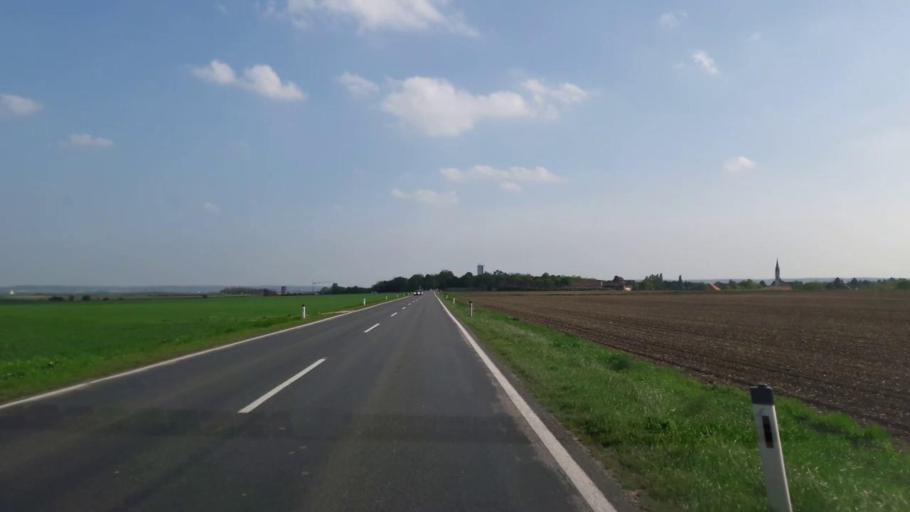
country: AT
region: Lower Austria
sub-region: Politischer Bezirk Hollabrunn
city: Guntersdorf
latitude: 48.6568
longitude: 16.0518
